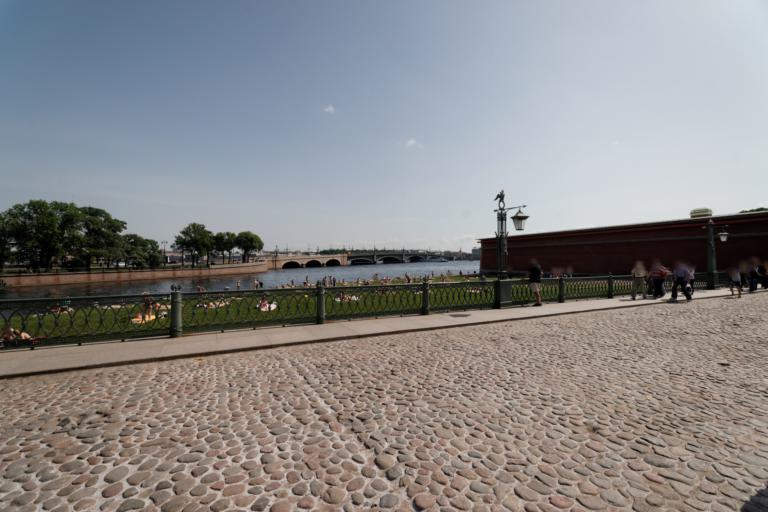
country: RU
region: St.-Petersburg
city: Saint Petersburg
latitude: 59.9517
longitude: 30.3221
